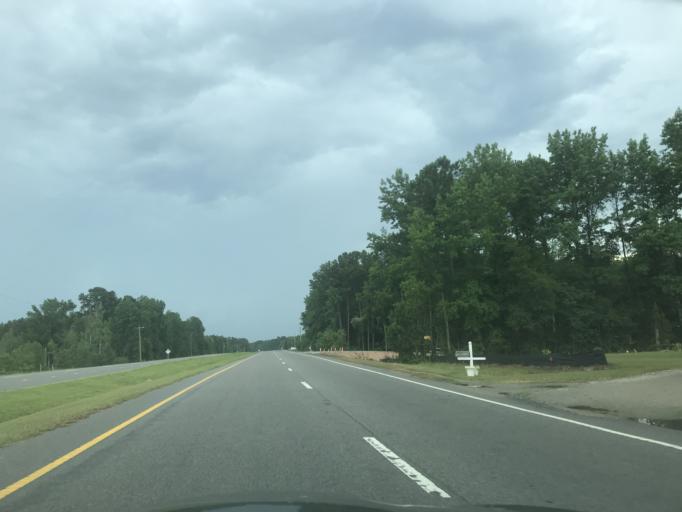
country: US
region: North Carolina
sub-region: Johnston County
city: Wilsons Mills
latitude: 35.5847
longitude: -78.4034
